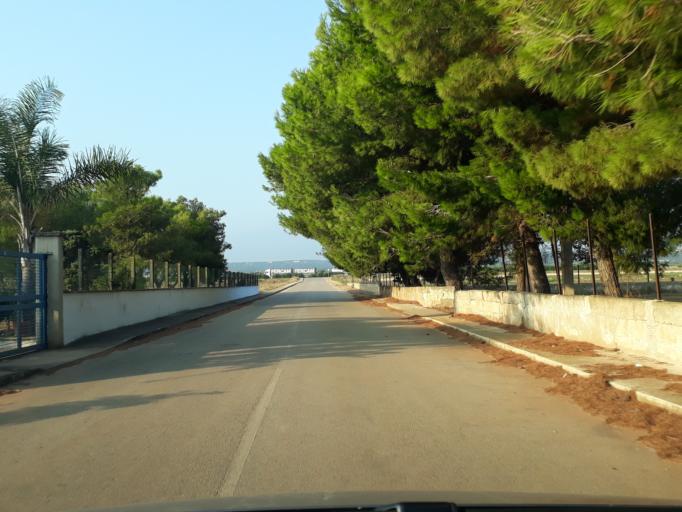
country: IT
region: Apulia
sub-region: Provincia di Brindisi
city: Carovigno
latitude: 40.7470
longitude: 17.7120
